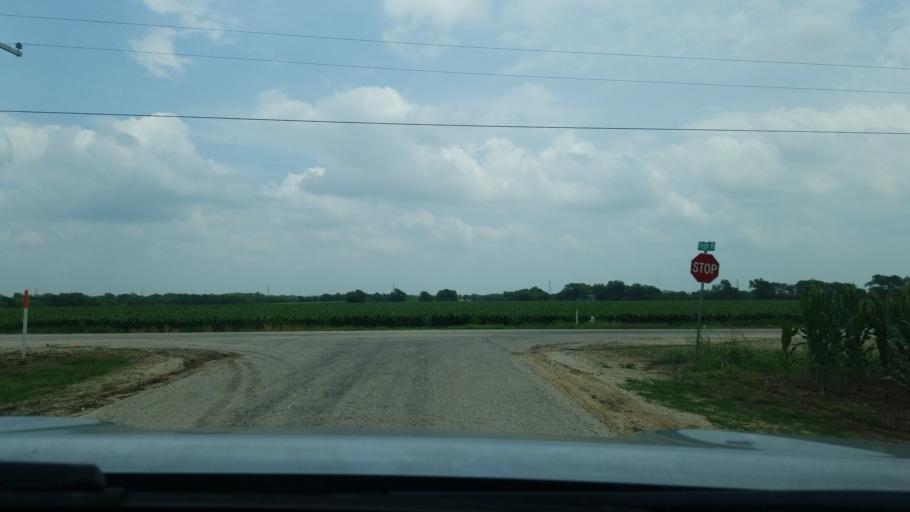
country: US
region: Texas
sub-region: Guadalupe County
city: Geronimo
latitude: 29.6802
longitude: -98.0033
